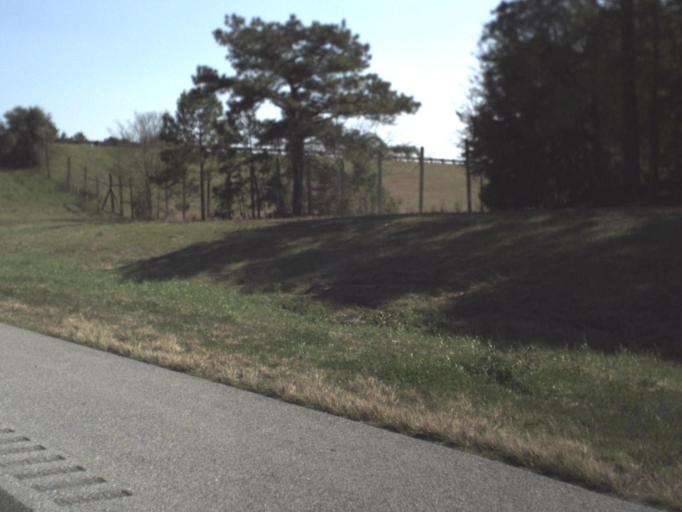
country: US
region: Florida
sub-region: Jackson County
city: Sneads
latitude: 30.6487
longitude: -85.0135
